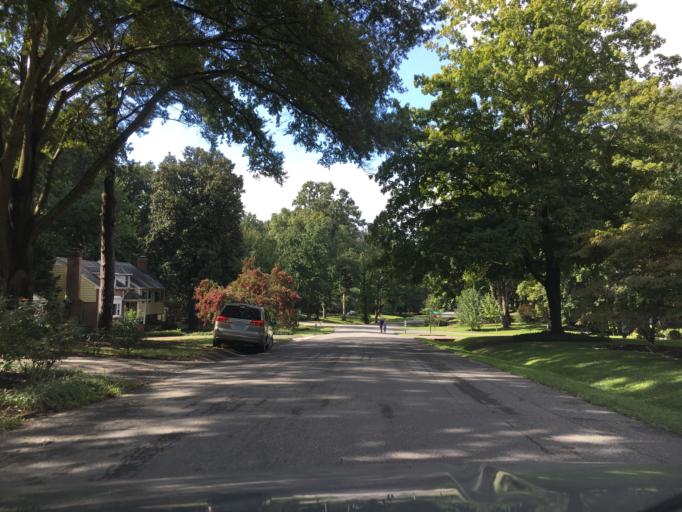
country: US
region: Virginia
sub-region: Henrico County
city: Tuckahoe
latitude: 37.5857
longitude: -77.5391
